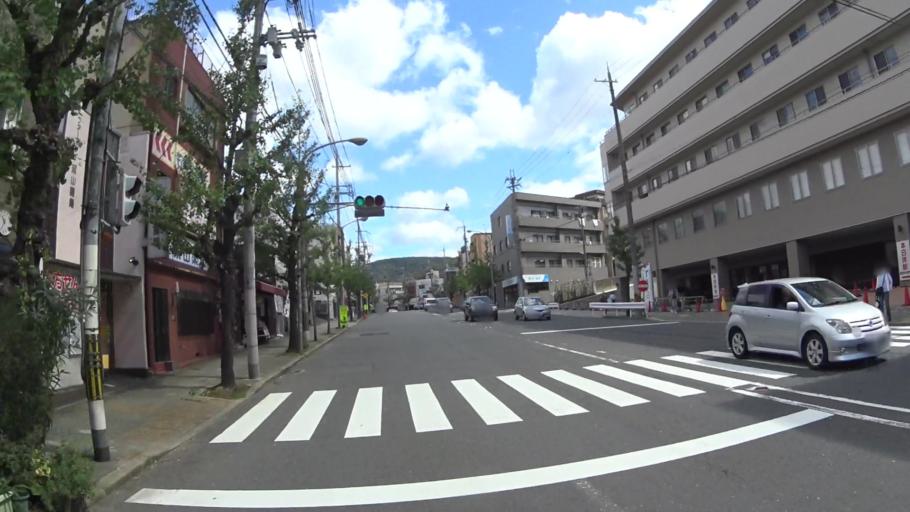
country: JP
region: Kyoto
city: Kyoto
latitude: 34.9816
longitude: 135.7726
